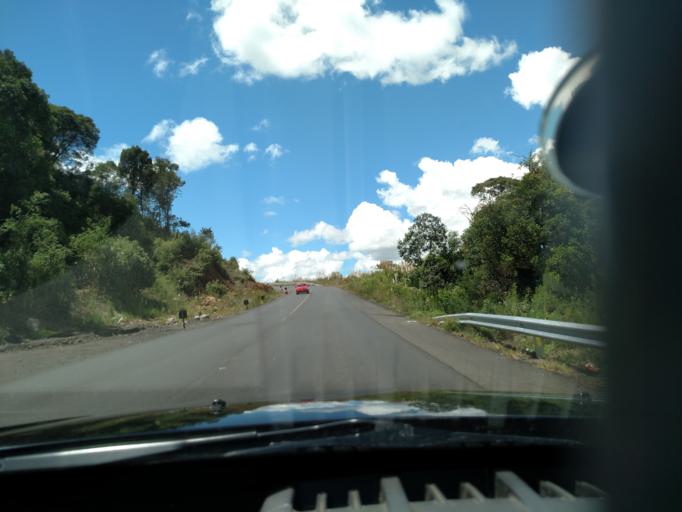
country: BR
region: Santa Catarina
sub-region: Sao Joaquim
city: Sao Joaquim
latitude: -28.2441
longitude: -49.9685
